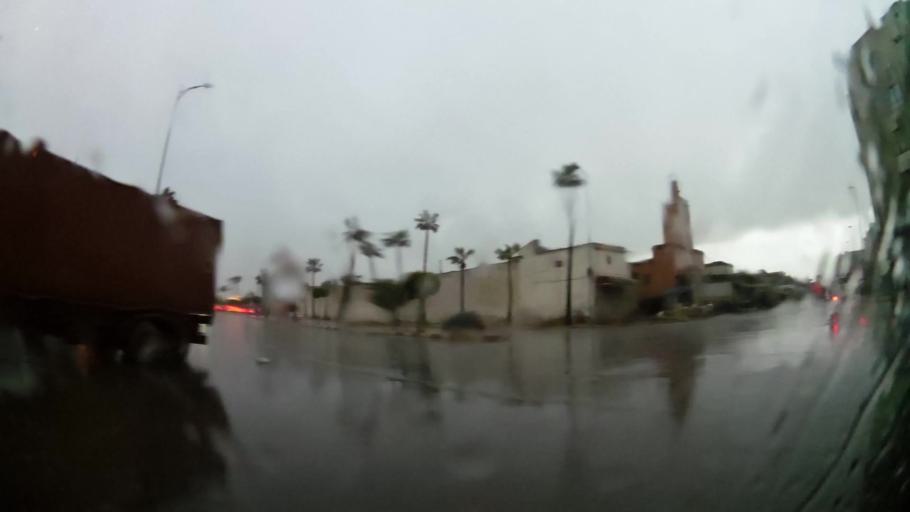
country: MA
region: Grand Casablanca
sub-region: Casablanca
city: Casablanca
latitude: 33.5623
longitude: -7.5972
